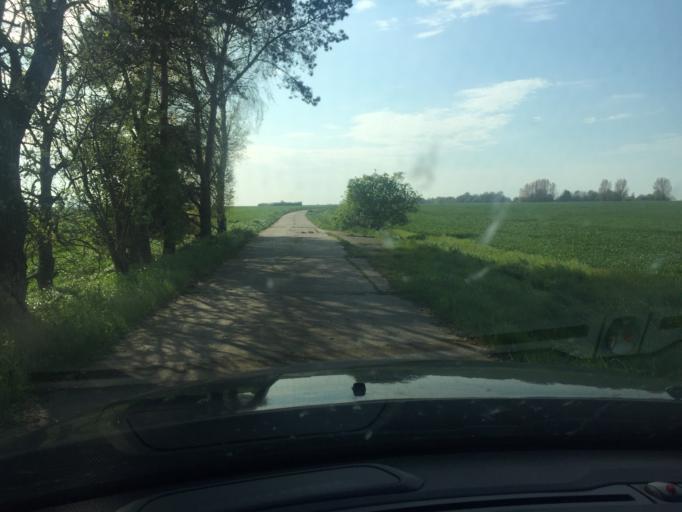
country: DE
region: Mecklenburg-Vorpommern
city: Saal
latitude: 54.3137
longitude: 12.4936
